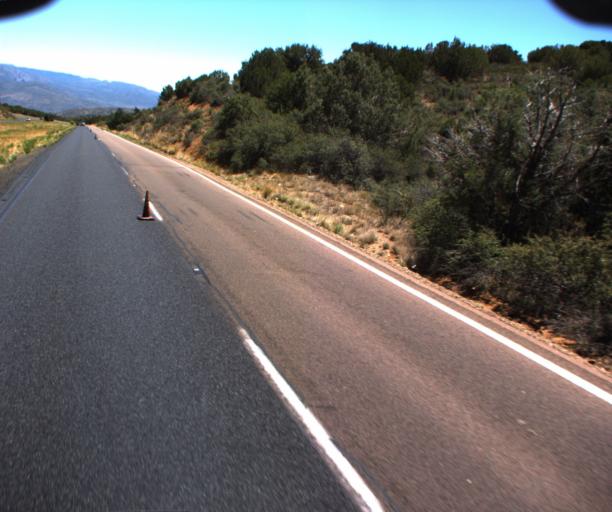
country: US
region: Arizona
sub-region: Gila County
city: Payson
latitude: 34.1696
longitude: -111.3360
